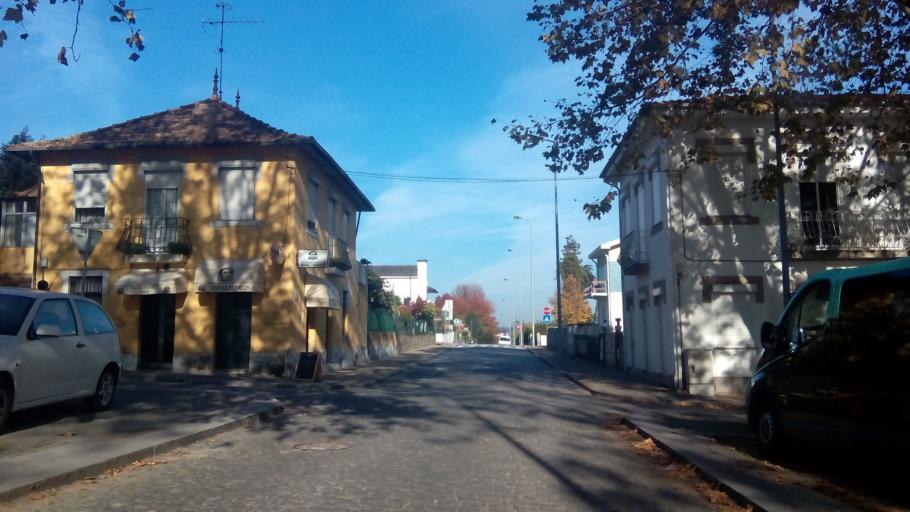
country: PT
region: Porto
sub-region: Paredes
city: Paredes
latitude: 41.2044
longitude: -8.3297
